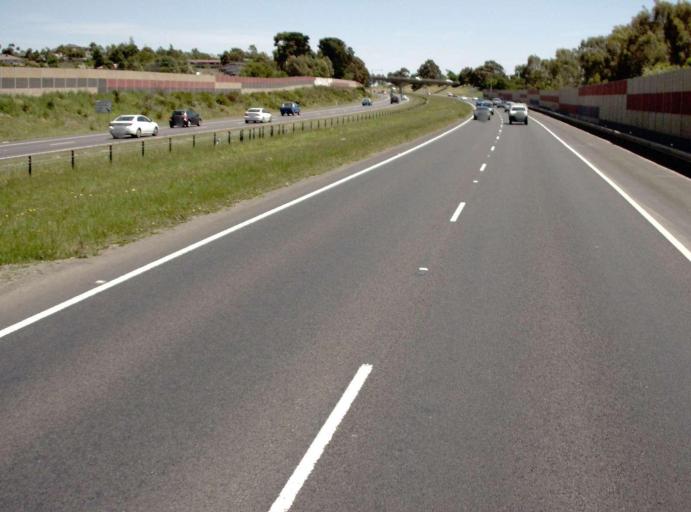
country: AU
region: Victoria
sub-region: Casey
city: Berwick
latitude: -38.0547
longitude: 145.3626
